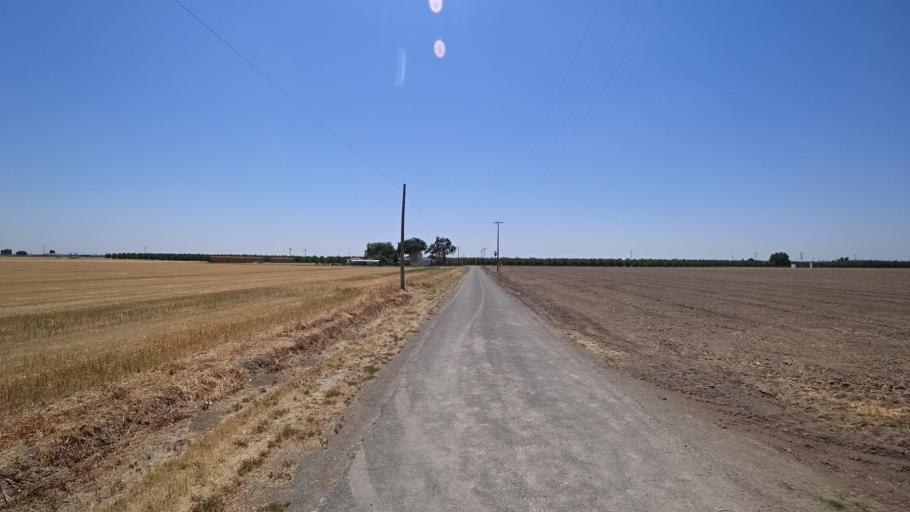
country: US
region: California
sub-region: Fresno County
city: Laton
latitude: 36.3884
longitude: -119.7367
